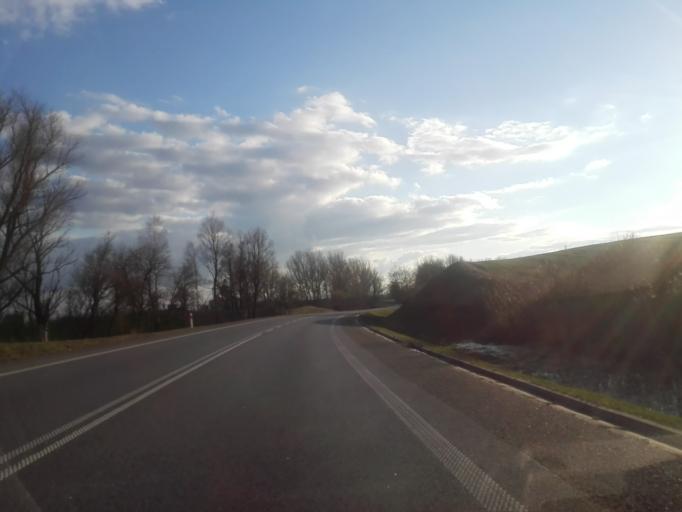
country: PL
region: Podlasie
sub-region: Suwalki
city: Suwalki
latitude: 54.1978
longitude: 23.0187
